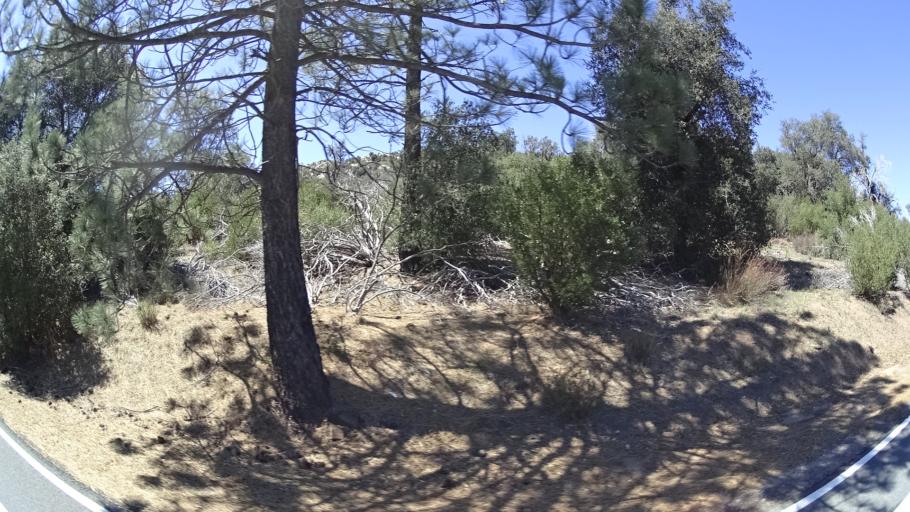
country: US
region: California
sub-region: San Diego County
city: Descanso
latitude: 32.9260
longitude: -116.5638
